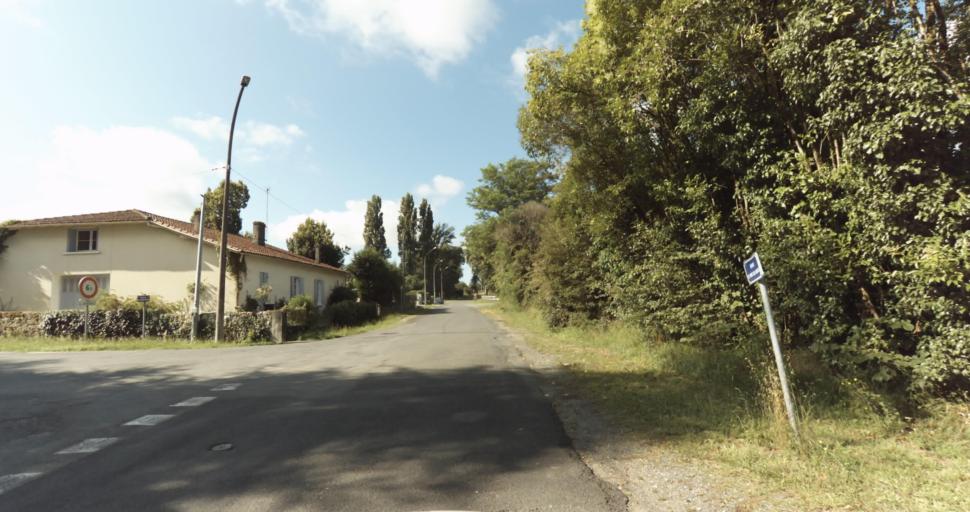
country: FR
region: Aquitaine
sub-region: Departement de la Gironde
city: Bazas
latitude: 44.4269
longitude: -0.2138
